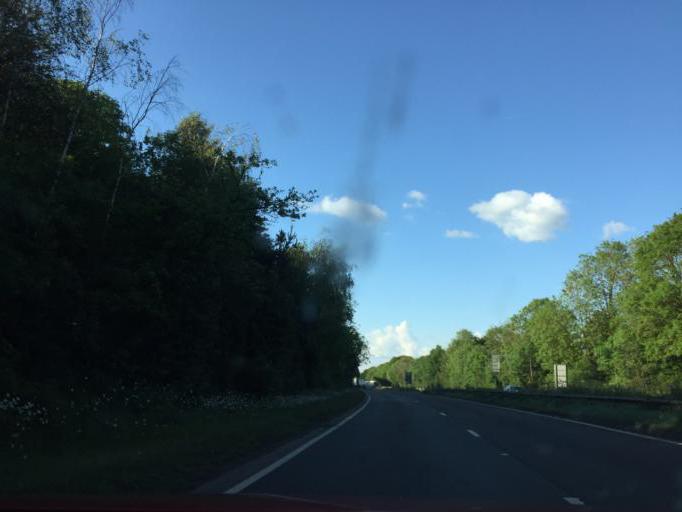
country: GB
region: England
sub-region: Warwickshire
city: Exhall
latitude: 52.4658
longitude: -1.4920
